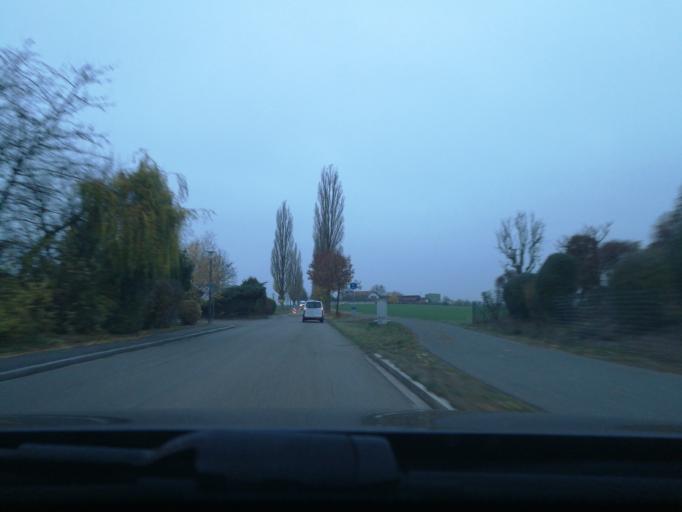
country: DE
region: Bavaria
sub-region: Regierungsbezirk Mittelfranken
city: Obermichelbach
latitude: 49.5158
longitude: 10.9235
